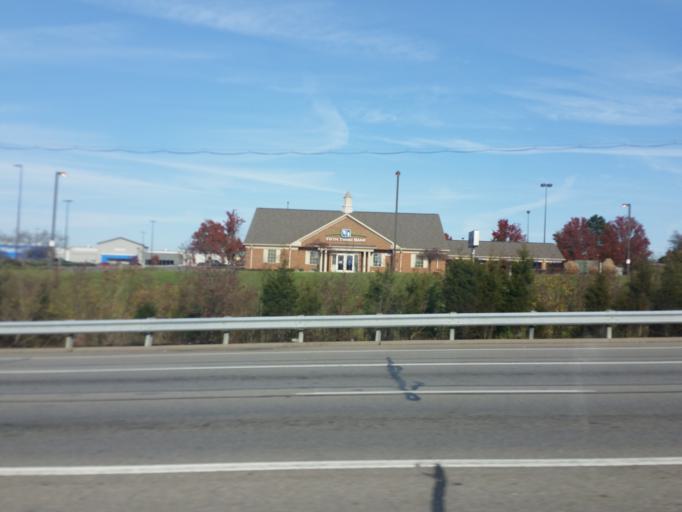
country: US
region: Kentucky
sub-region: Campbell County
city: Alexandria
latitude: 38.9854
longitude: -84.4025
